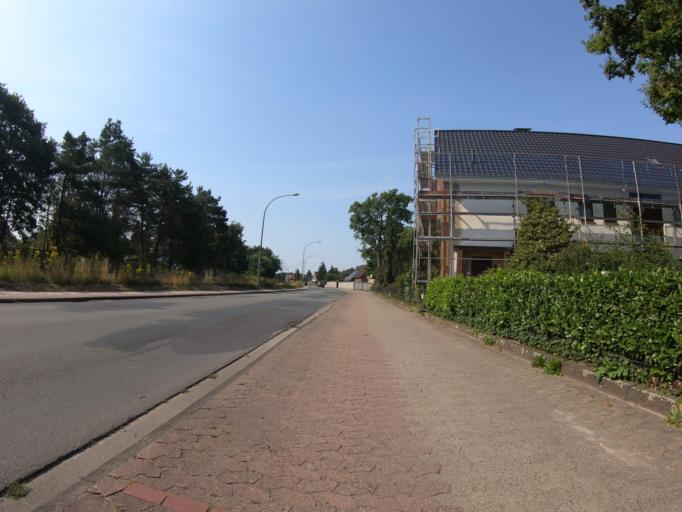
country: DE
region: Lower Saxony
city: Gifhorn
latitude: 52.4765
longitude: 10.5352
